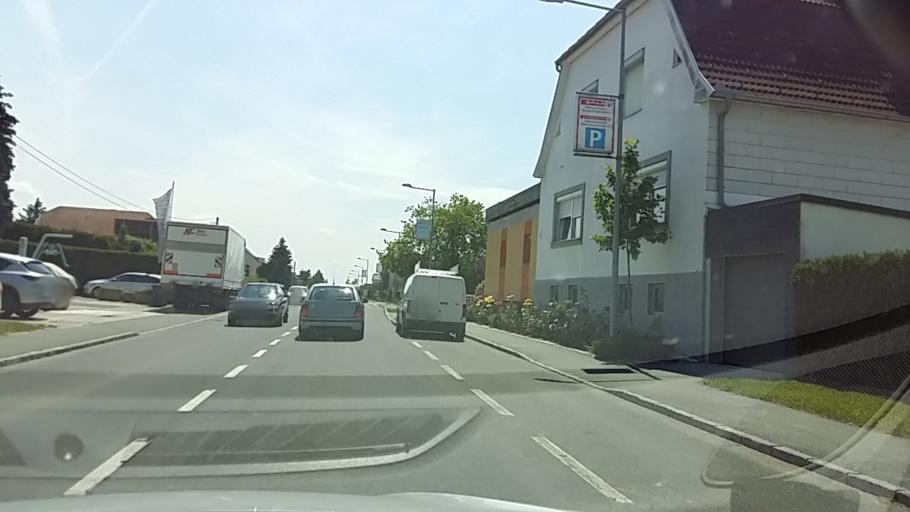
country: AT
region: Burgenland
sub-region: Politischer Bezirk Oberpullendorf
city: Oberpullendorf
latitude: 47.5043
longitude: 16.5074
